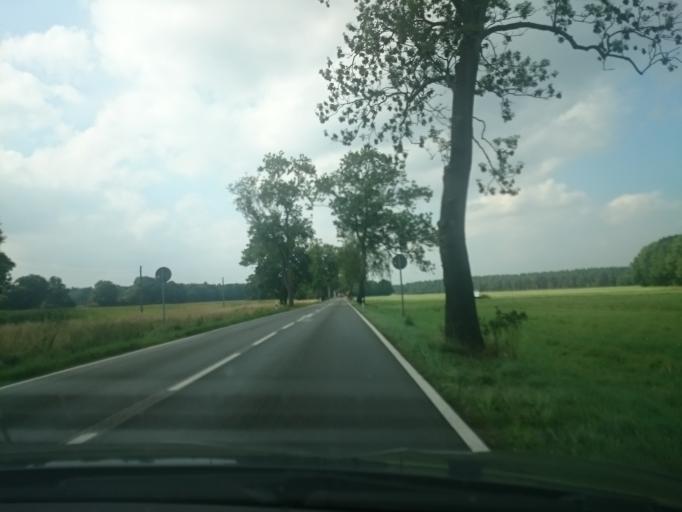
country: DE
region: Mecklenburg-Vorpommern
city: Ducherow
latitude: 53.7165
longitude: 13.8325
